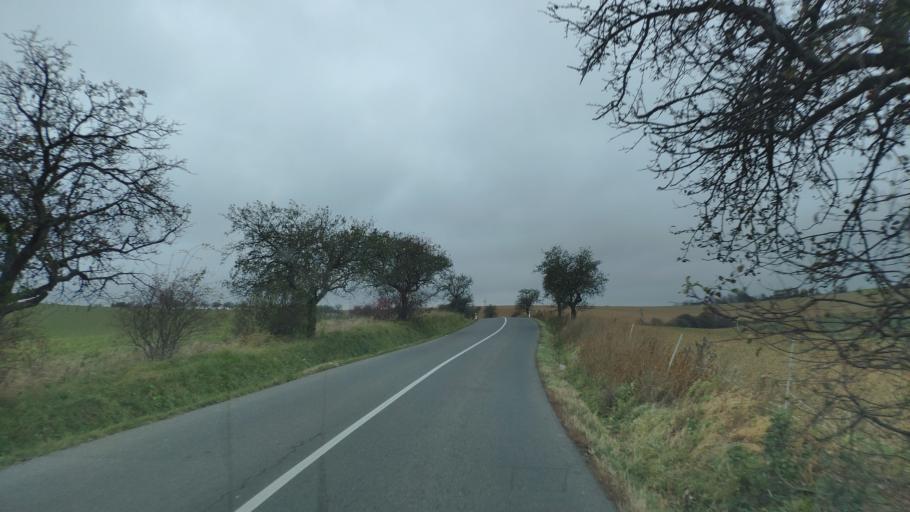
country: SK
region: Presovsky
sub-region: Okres Presov
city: Presov
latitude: 49.0982
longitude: 21.2282
